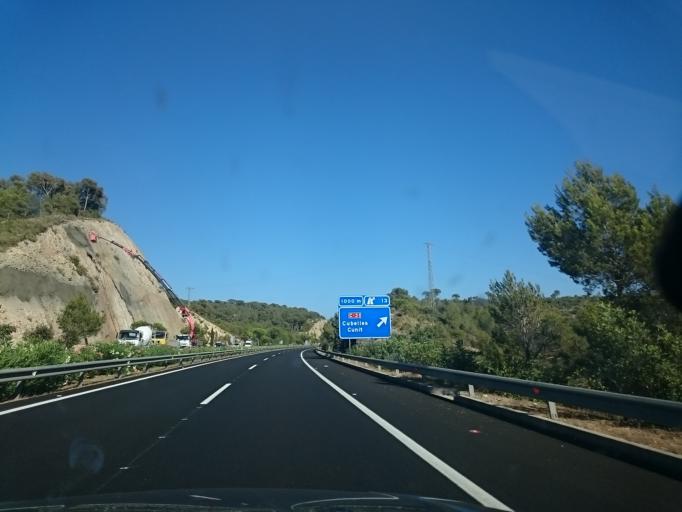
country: ES
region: Catalonia
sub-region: Provincia de Tarragona
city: Cunit
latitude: 41.2138
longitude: 1.6351
